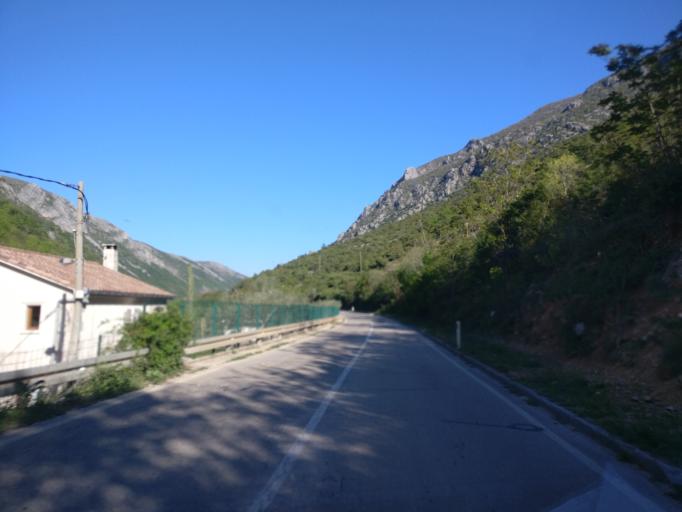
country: BA
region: Federation of Bosnia and Herzegovina
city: Stolac
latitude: 43.0748
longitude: 18.0290
